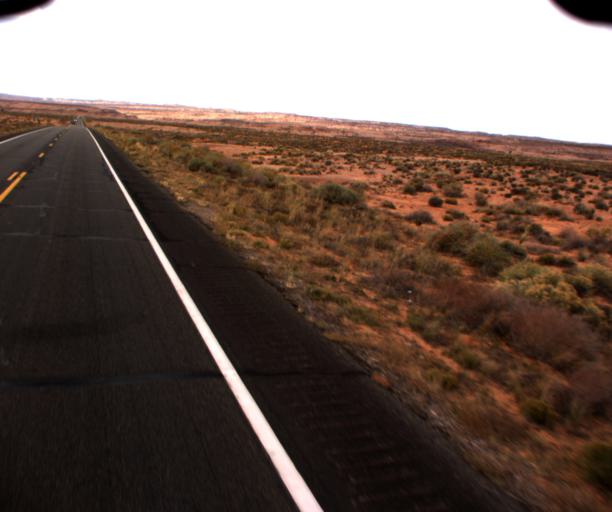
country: US
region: Arizona
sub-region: Apache County
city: Many Farms
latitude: 36.9400
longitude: -109.6758
